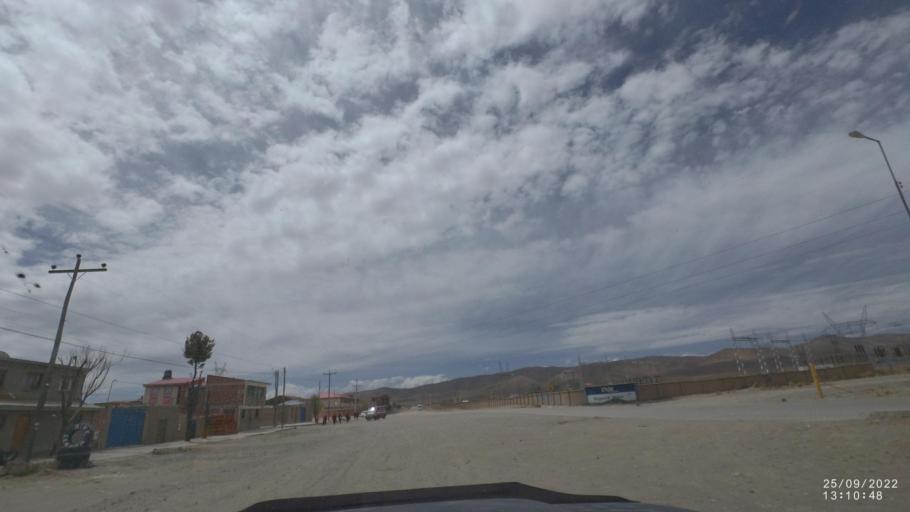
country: BO
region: Oruro
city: Oruro
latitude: -17.9696
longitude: -67.0479
